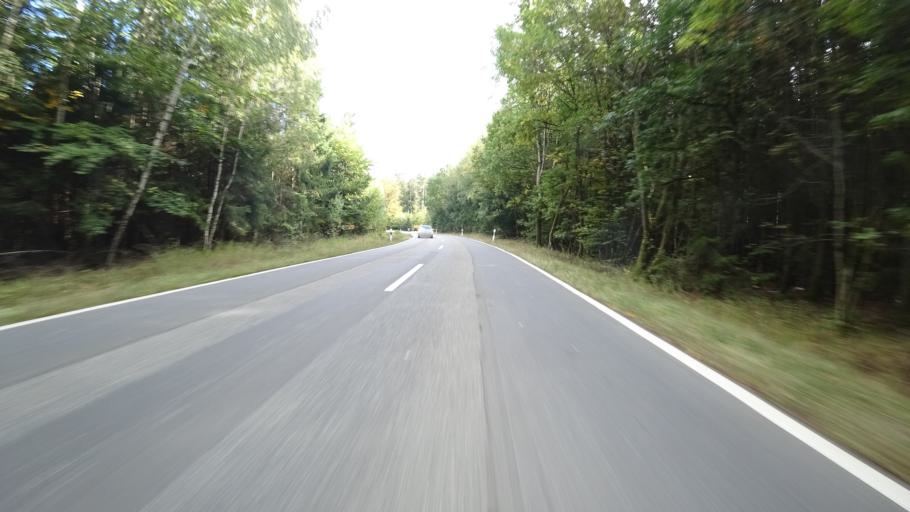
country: DE
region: Rheinland-Pfalz
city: Morschbach
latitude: 50.0075
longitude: 7.6372
